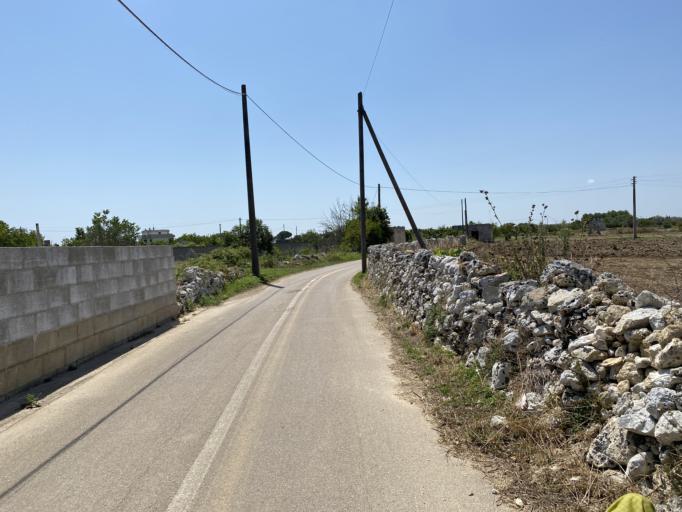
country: IT
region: Apulia
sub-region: Provincia di Lecce
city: Giuggianello
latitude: 40.0983
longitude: 18.3643
